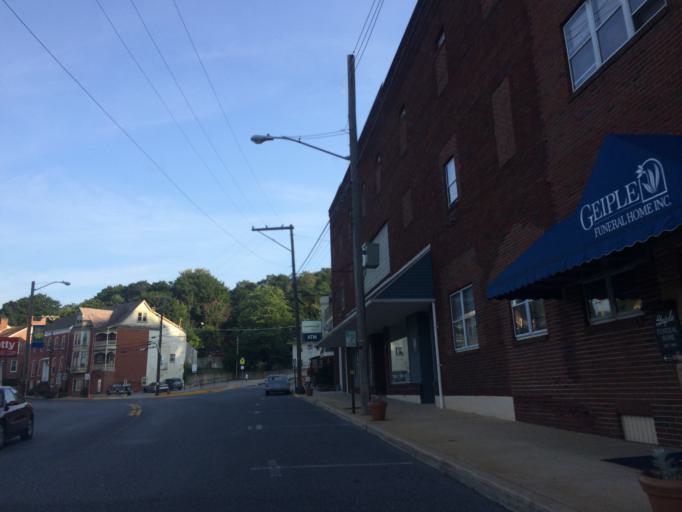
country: US
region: Pennsylvania
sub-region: York County
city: Glen Rock
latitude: 39.7942
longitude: -76.7314
